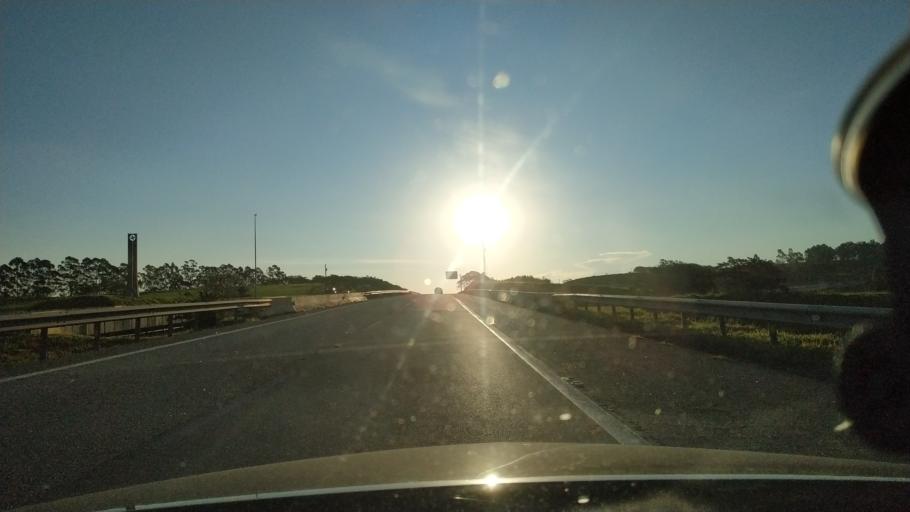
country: BR
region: Sao Paulo
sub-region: Sao Jose Dos Campos
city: Sao Jose dos Campos
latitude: -23.2665
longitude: -45.8189
